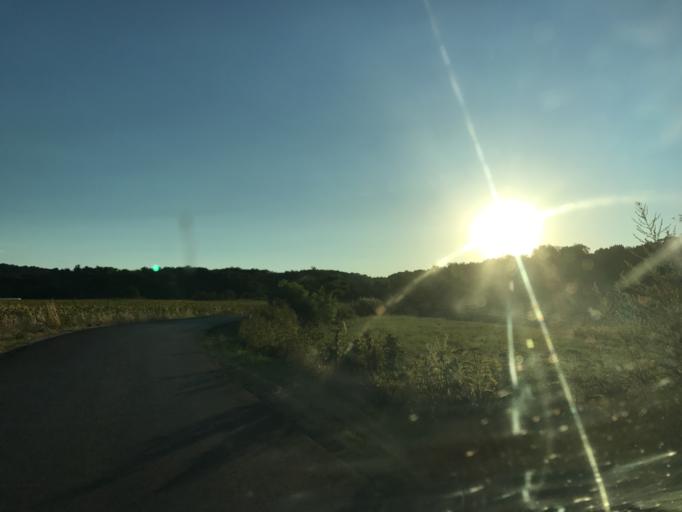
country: BG
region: Vidin
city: Bregovo
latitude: 44.1219
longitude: 22.5757
